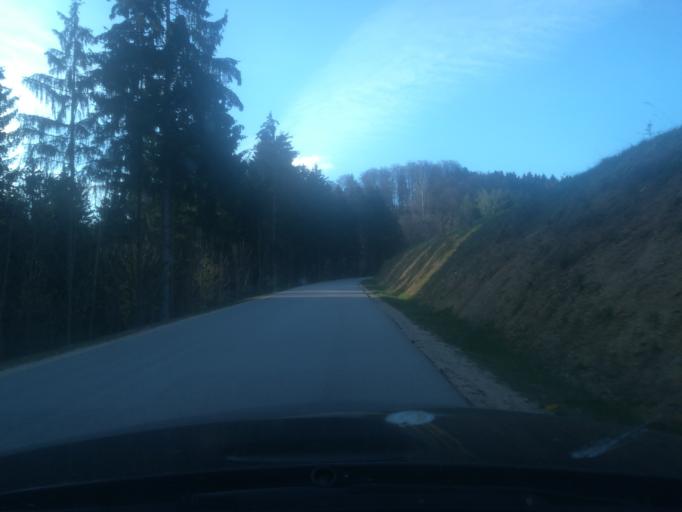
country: AT
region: Upper Austria
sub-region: Politischer Bezirk Perg
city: Bad Kreuzen
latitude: 48.2935
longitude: 14.7732
